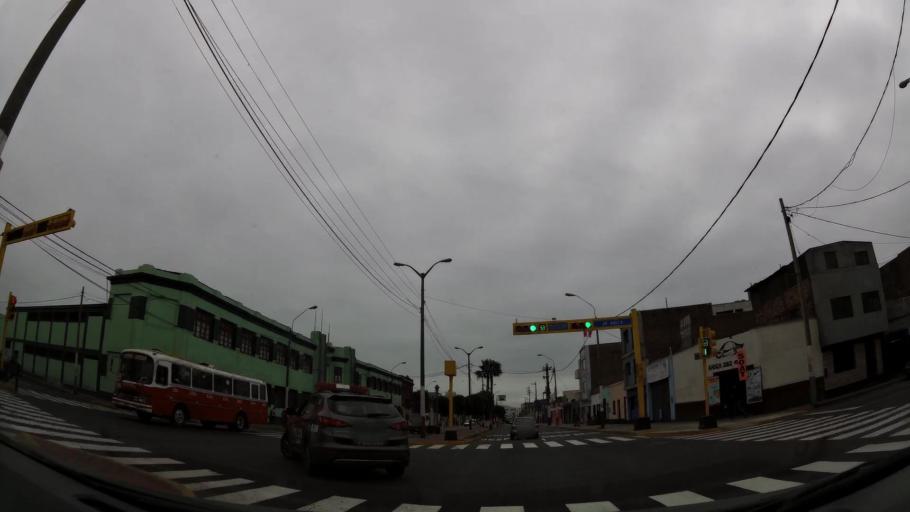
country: PE
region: Callao
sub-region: Callao
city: Callao
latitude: -12.0615
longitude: -77.1353
